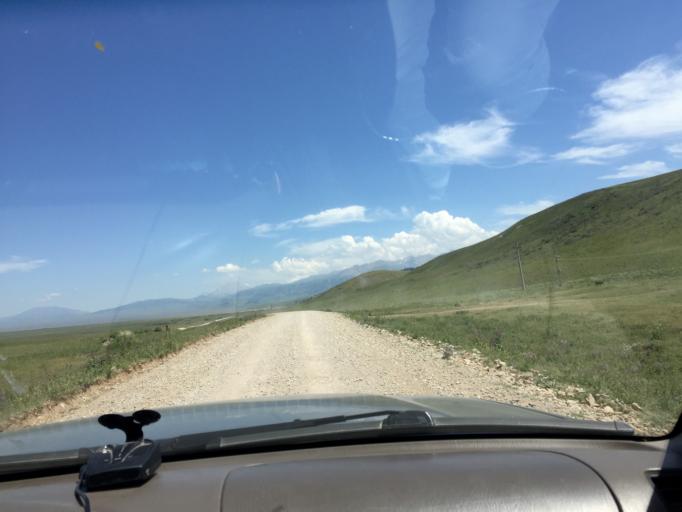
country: KZ
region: Almaty Oblysy
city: Kegen
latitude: 42.7693
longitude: 79.0875
